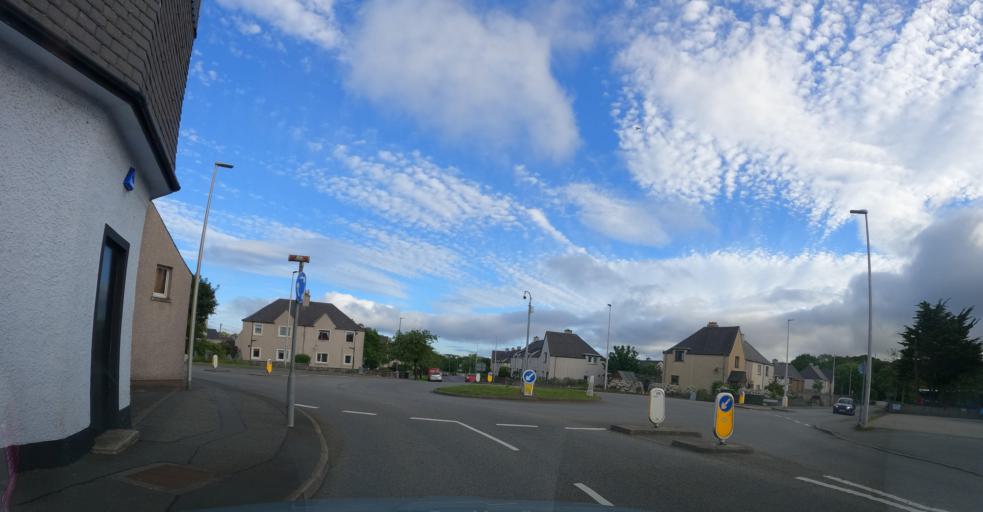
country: GB
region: Scotland
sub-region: Eilean Siar
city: Isle of Lewis
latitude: 58.2196
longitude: -6.3861
